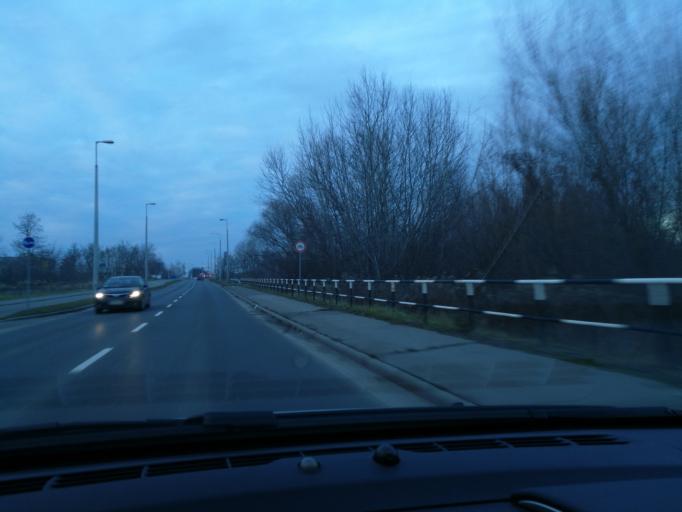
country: HU
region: Szabolcs-Szatmar-Bereg
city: Nyiregyhaza
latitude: 47.9671
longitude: 21.7421
